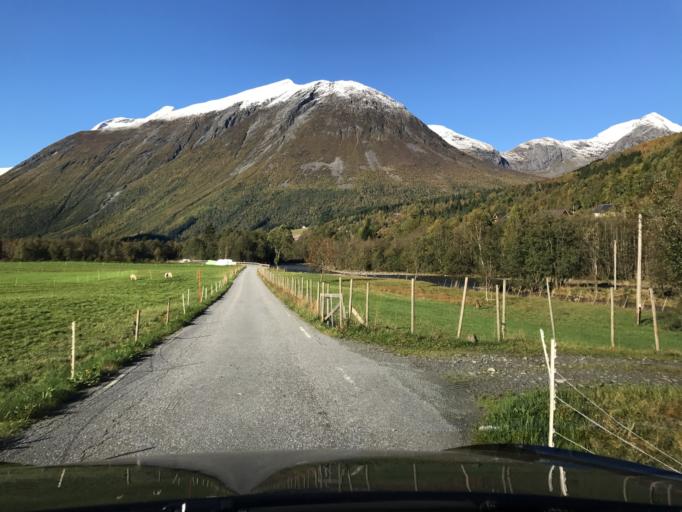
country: NO
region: More og Romsdal
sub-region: Norddal
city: Valldal
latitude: 62.3306
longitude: 7.3777
